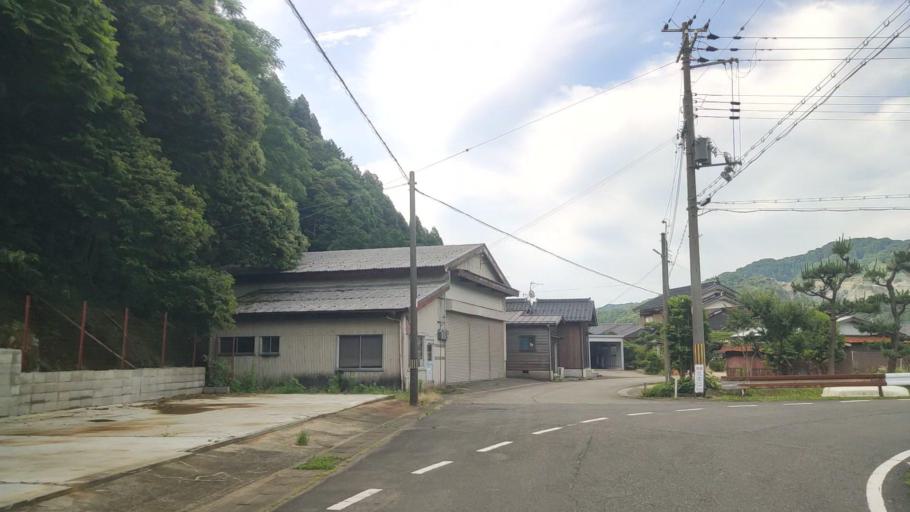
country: JP
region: Hyogo
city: Toyooka
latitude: 35.6388
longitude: 134.8402
